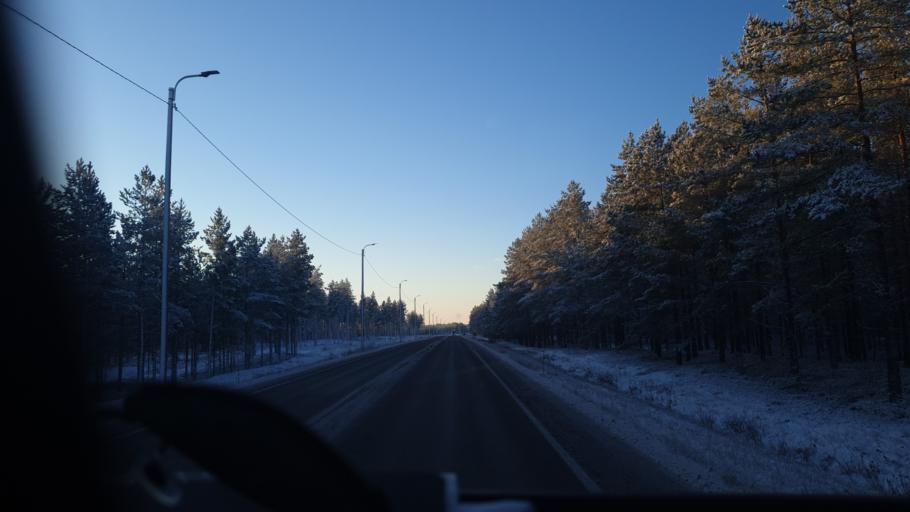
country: FI
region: Northern Ostrobothnia
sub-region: Ylivieska
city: Kalajoki
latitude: 64.2353
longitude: 23.8293
